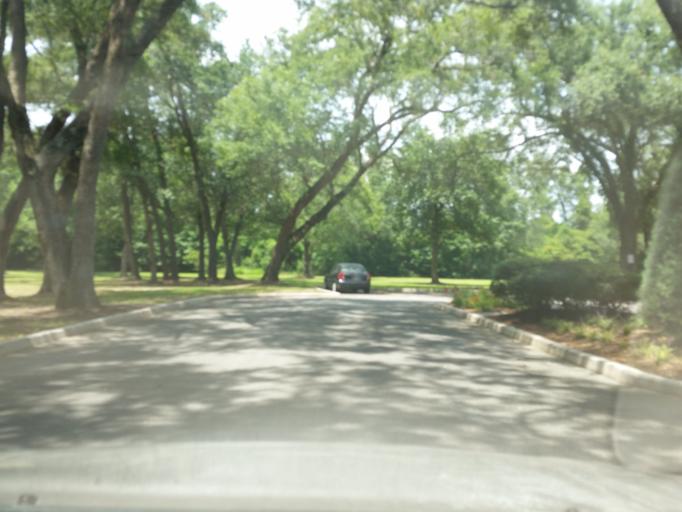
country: US
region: Florida
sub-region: Escambia County
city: Ferry Pass
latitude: 30.5017
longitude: -87.2182
